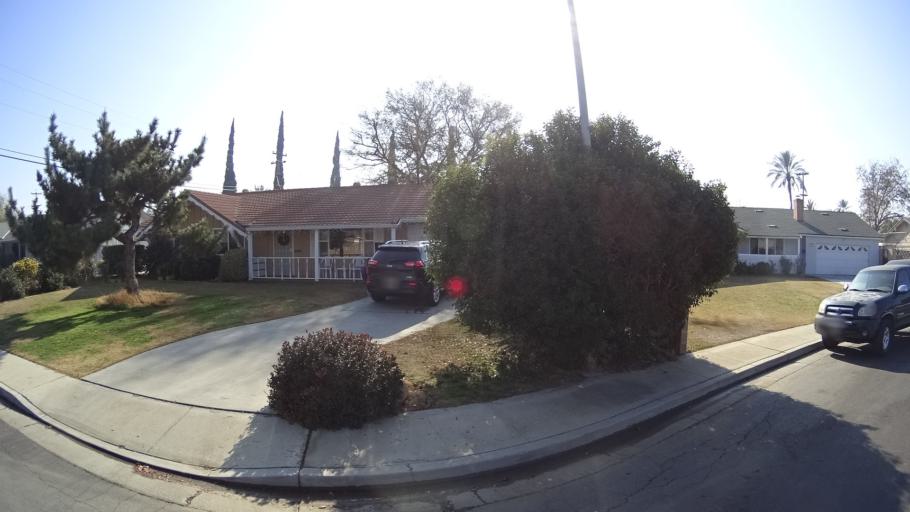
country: US
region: California
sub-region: Kern County
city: Bakersfield
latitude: 35.3456
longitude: -119.0641
